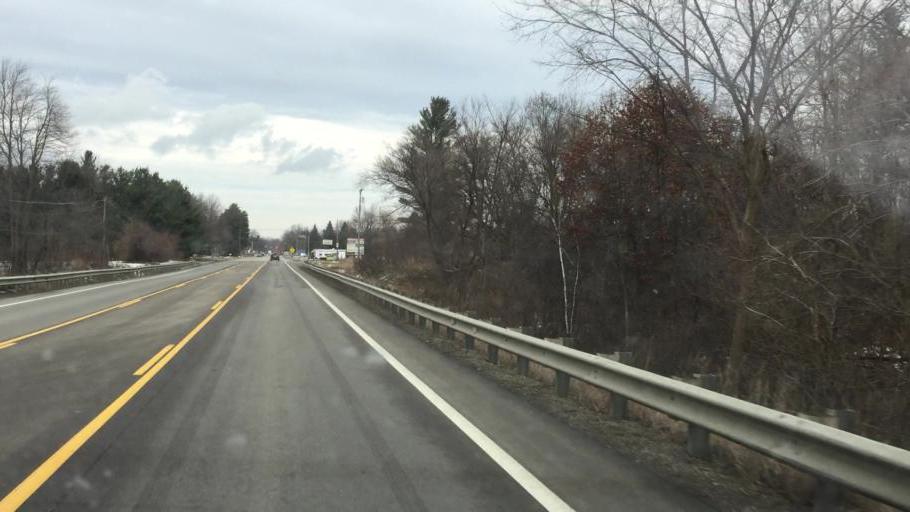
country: US
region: Michigan
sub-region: Lapeer County
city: Barnes Lake-Millers Lake
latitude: 43.1979
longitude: -83.3128
